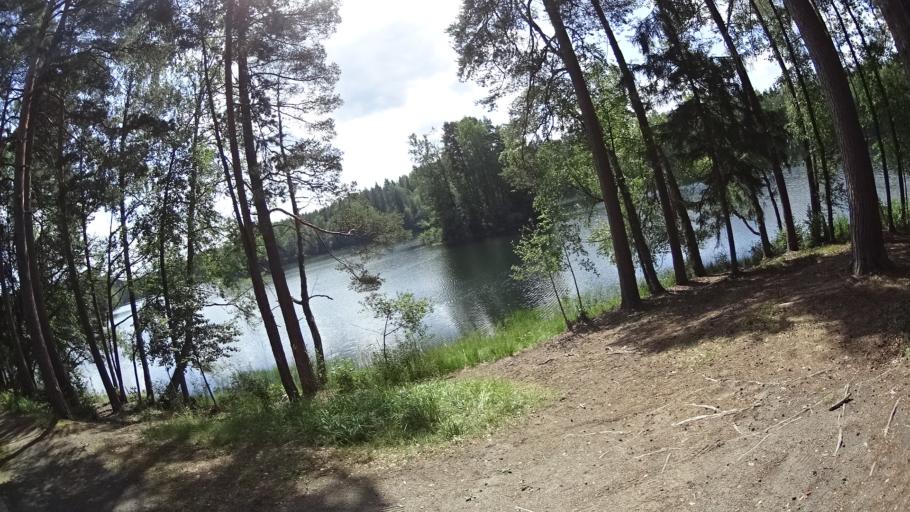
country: FI
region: Haeme
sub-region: Forssa
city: Tammela
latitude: 60.7760
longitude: 23.8465
